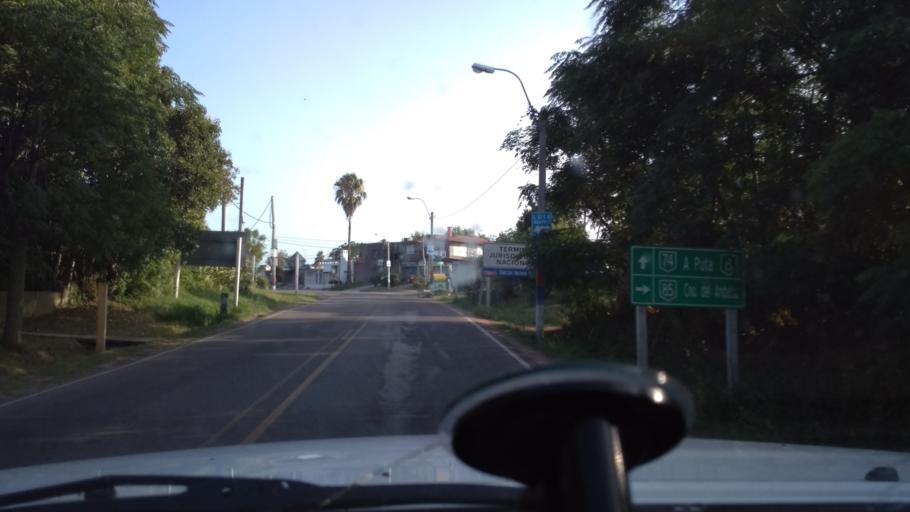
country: UY
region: Canelones
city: Joaquin Suarez
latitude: -34.7318
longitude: -56.0347
